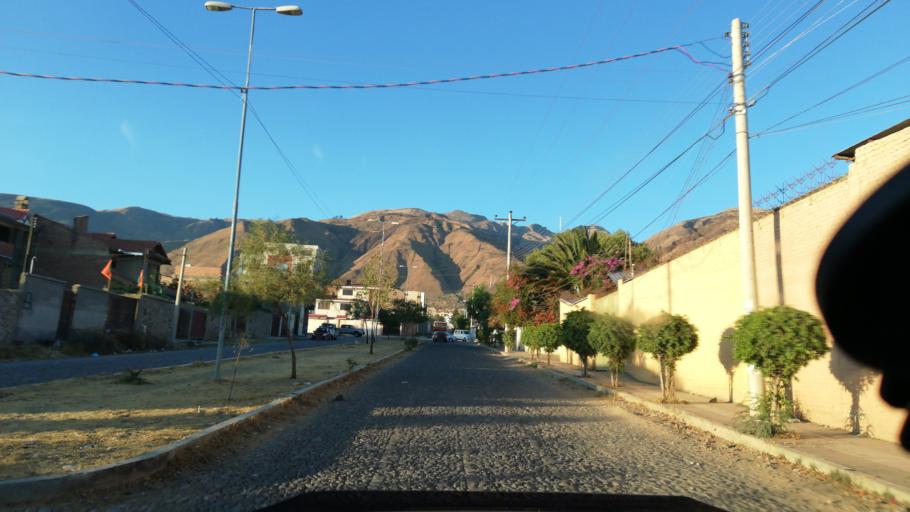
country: BO
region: Cochabamba
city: Cochabamba
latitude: -17.3464
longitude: -66.1970
